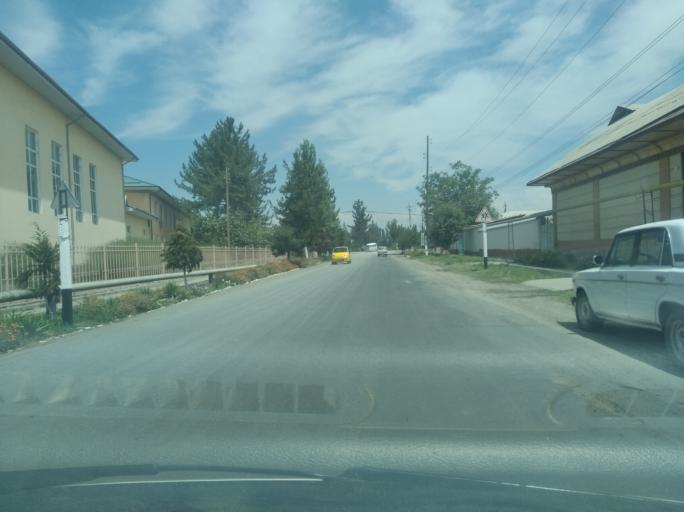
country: UZ
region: Andijon
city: Khujaobod
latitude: 40.6372
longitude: 72.4493
